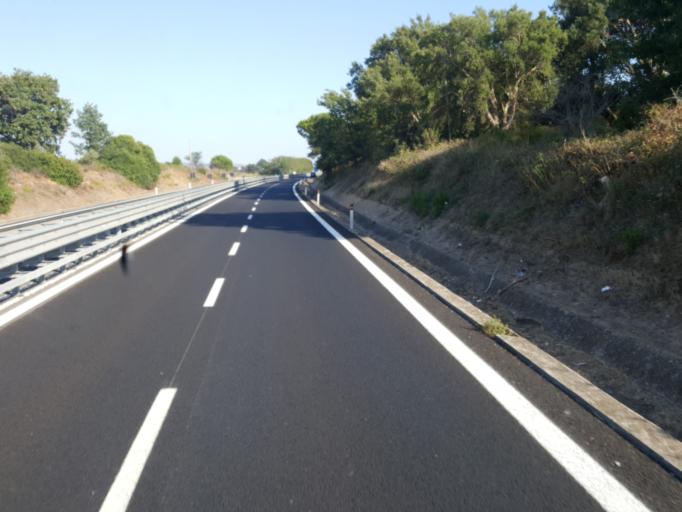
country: IT
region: Latium
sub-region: Provincia di Viterbo
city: Montalto di Castro
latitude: 42.3058
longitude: 11.6619
